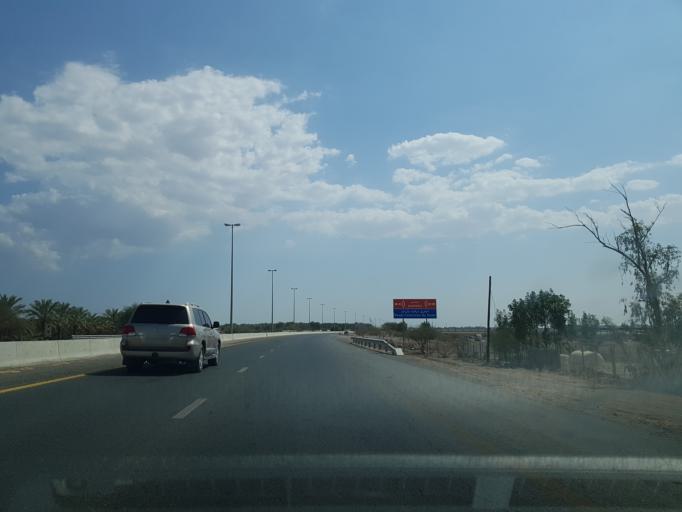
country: AE
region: Ash Shariqah
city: Adh Dhayd
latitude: 25.2404
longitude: 55.9155
